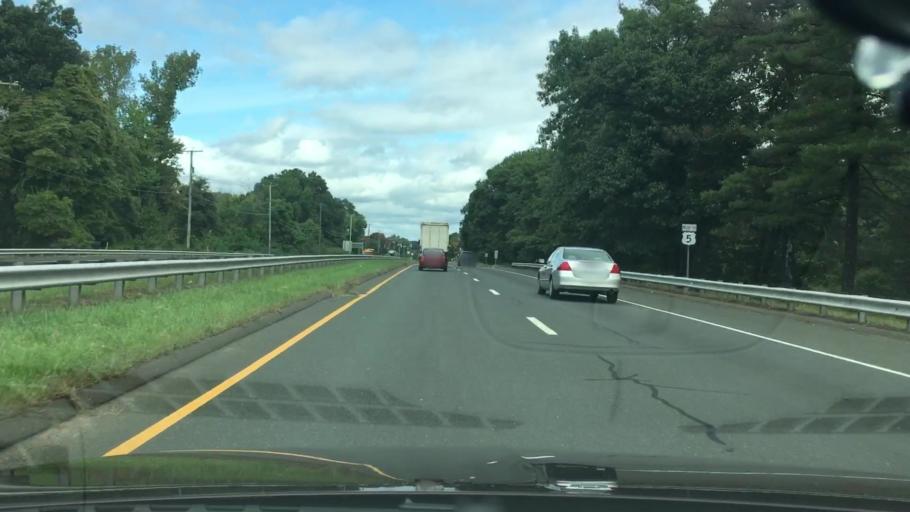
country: US
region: Connecticut
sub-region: Hartford County
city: South Windsor
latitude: 41.8086
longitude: -72.6134
